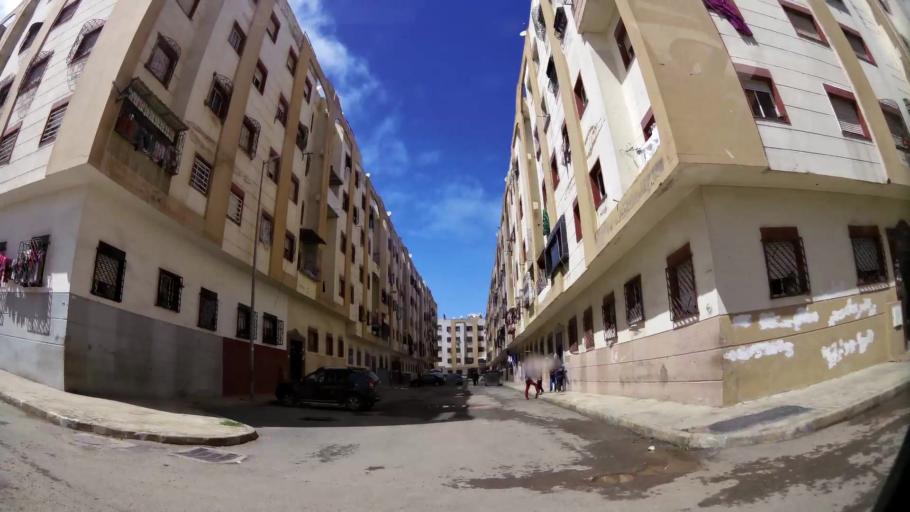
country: MA
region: Grand Casablanca
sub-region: Mediouna
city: Tit Mellil
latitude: 33.5996
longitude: -7.4792
